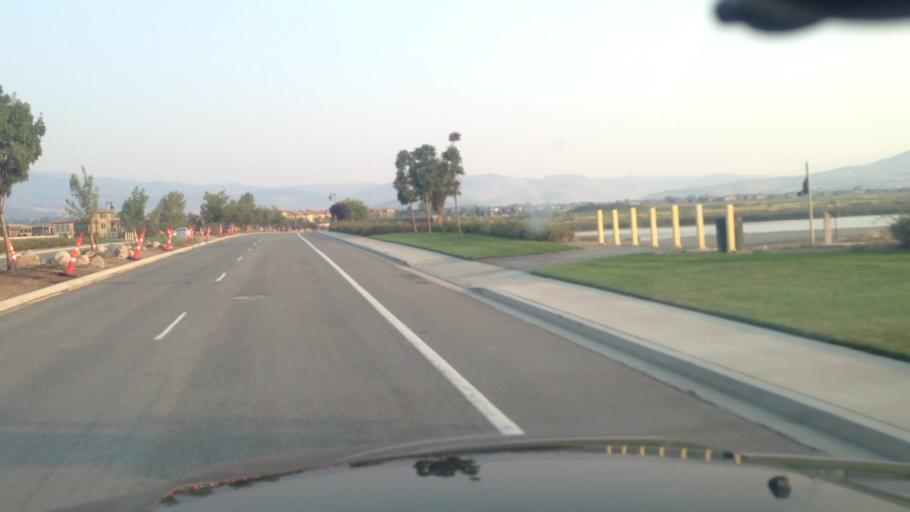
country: US
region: Nevada
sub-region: Washoe County
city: Sparks
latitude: 39.4218
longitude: -119.7329
